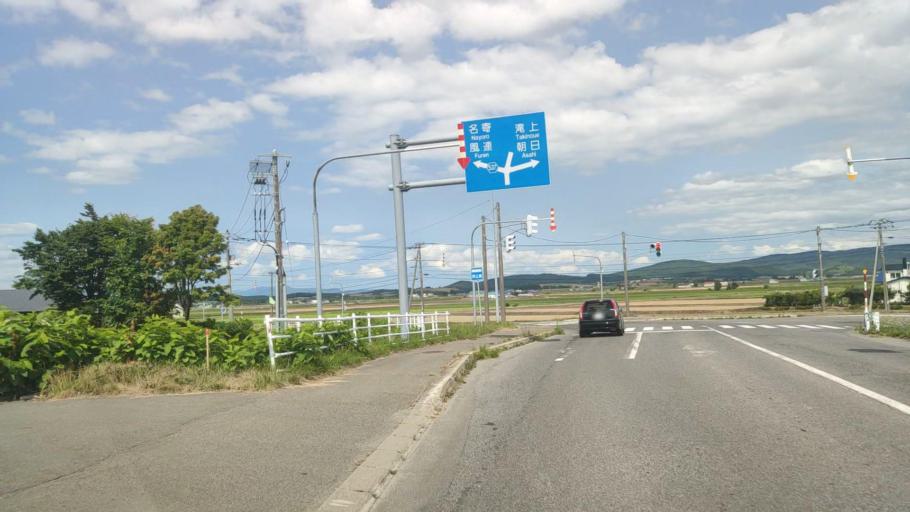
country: JP
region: Hokkaido
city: Nayoro
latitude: 44.1908
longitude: 142.4154
